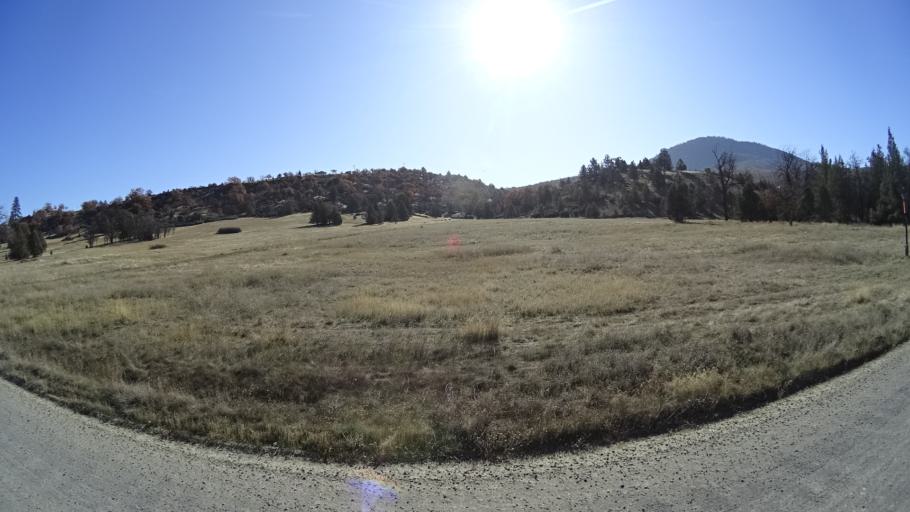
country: US
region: California
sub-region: Siskiyou County
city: Montague
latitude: 41.8971
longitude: -122.5174
